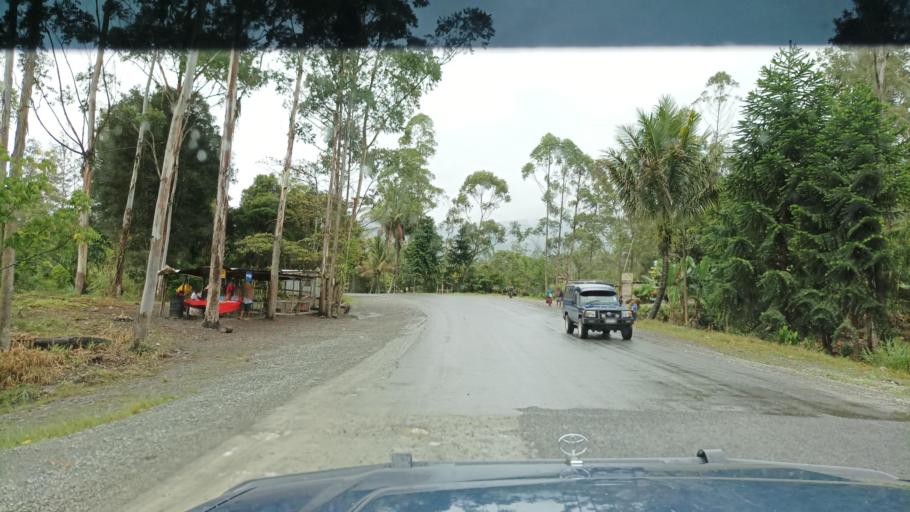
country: PG
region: Jiwaka
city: Minj
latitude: -5.8610
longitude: 144.6378
